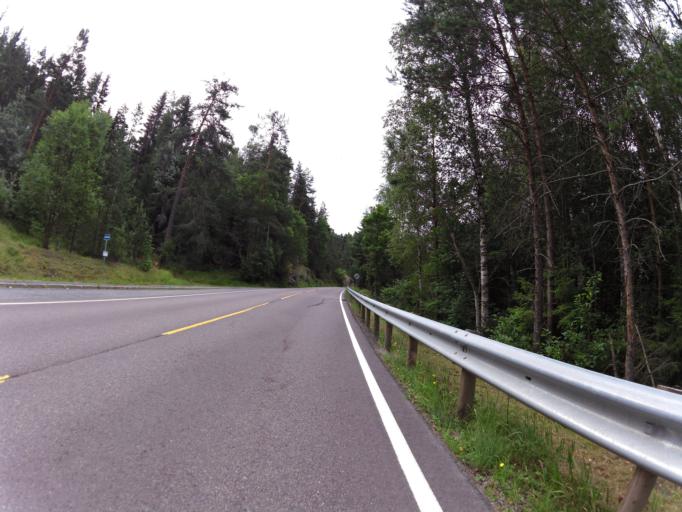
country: NO
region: Akershus
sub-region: Oppegard
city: Kolbotn
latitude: 59.8199
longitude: 10.7729
